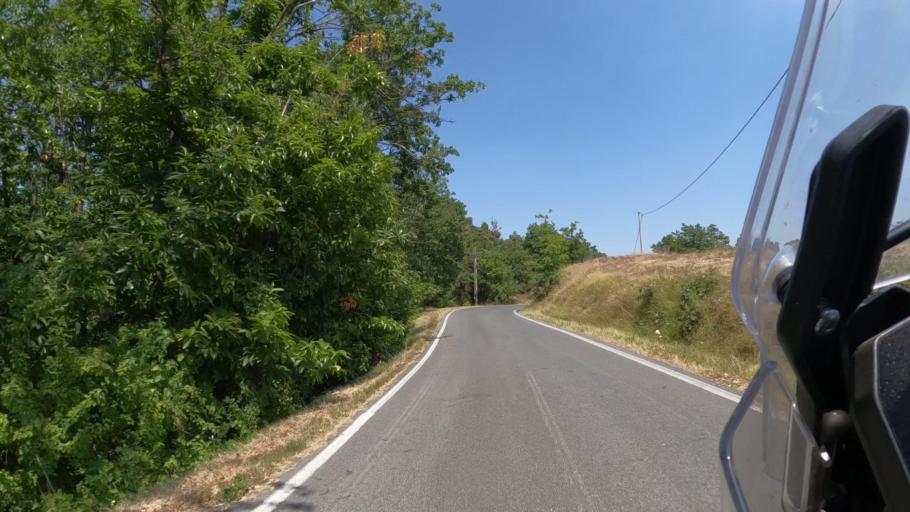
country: IT
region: Piedmont
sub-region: Provincia di Alessandria
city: Morbello
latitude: 44.5604
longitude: 8.5143
